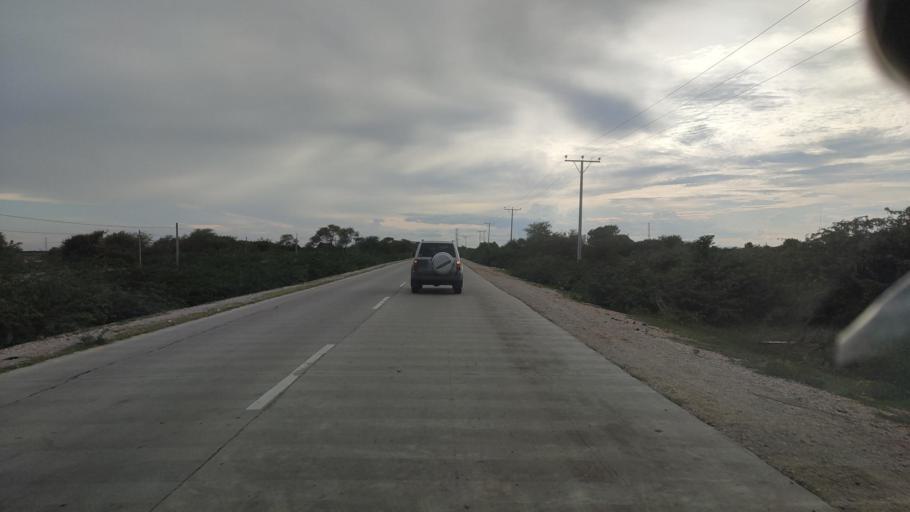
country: MM
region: Mandalay
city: Kyaukse
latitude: 21.3473
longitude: 96.1046
